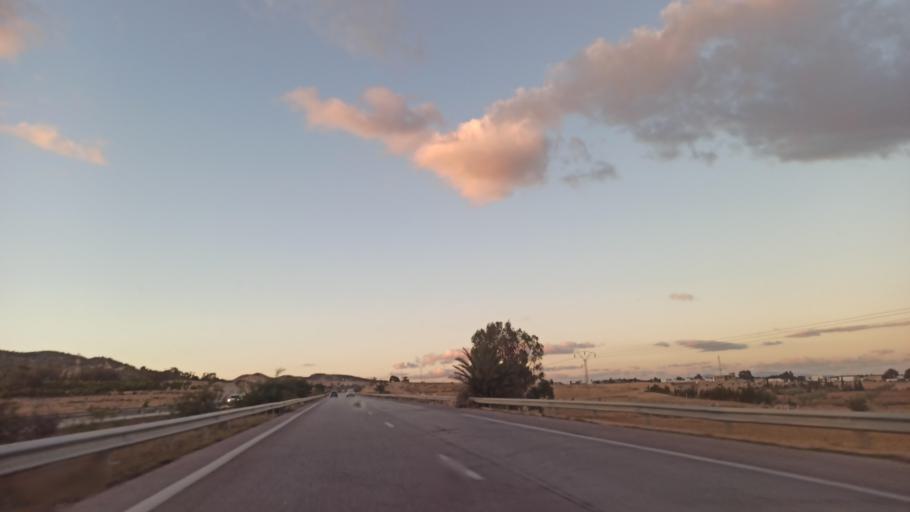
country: TN
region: Susah
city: Harqalah
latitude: 36.2241
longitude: 10.4160
